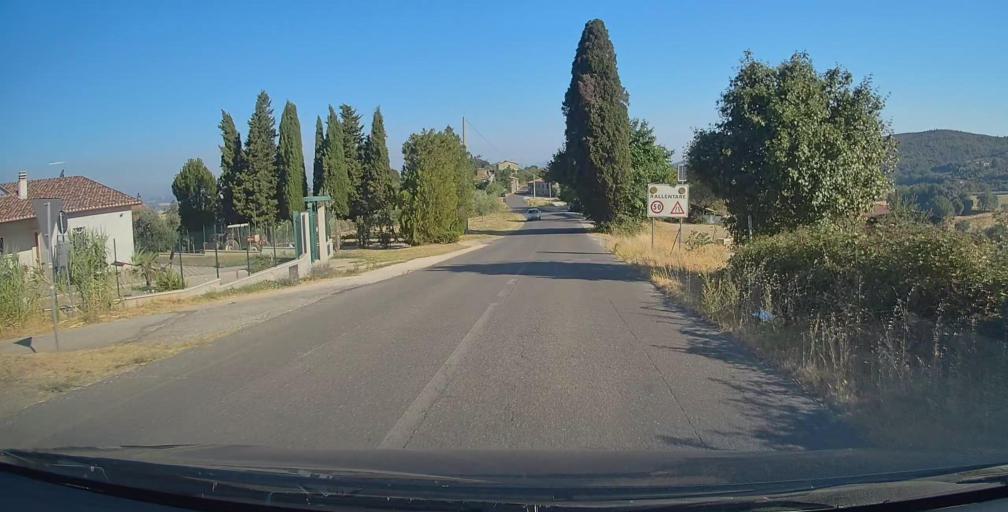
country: IT
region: Umbria
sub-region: Provincia di Terni
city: Calvi dell'Umbria
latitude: 42.4084
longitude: 12.5595
